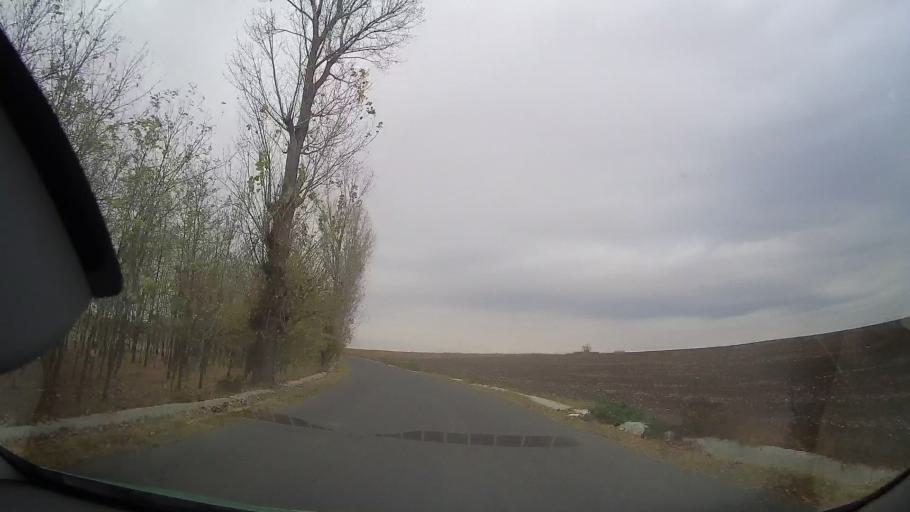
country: RO
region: Braila
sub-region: Comuna Ciocile
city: Ciocile
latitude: 44.7898
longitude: 27.2753
